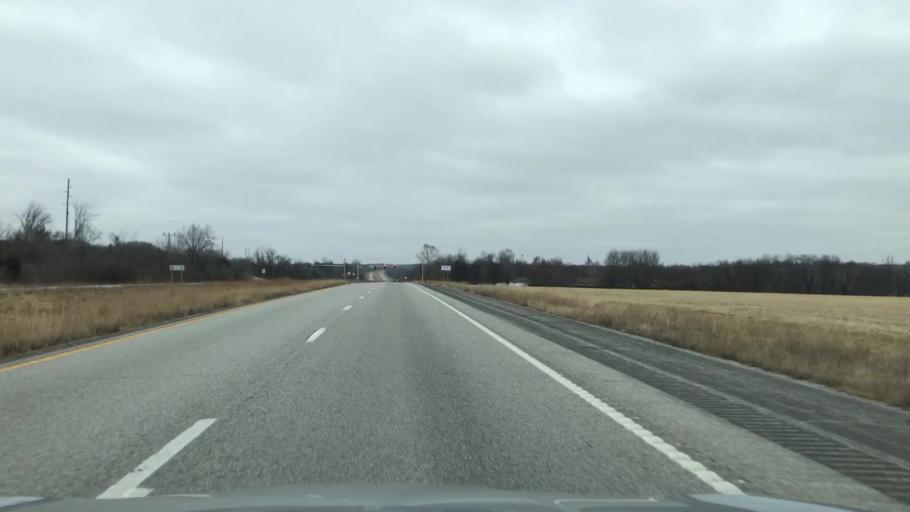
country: US
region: Missouri
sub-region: Clay County
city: Liberty
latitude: 39.2036
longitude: -94.4036
